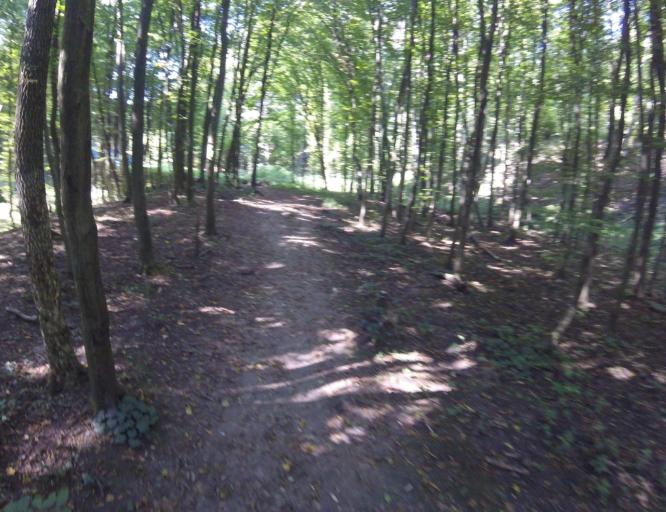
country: HU
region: Pest
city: Csobanka
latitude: 47.7045
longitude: 18.9811
